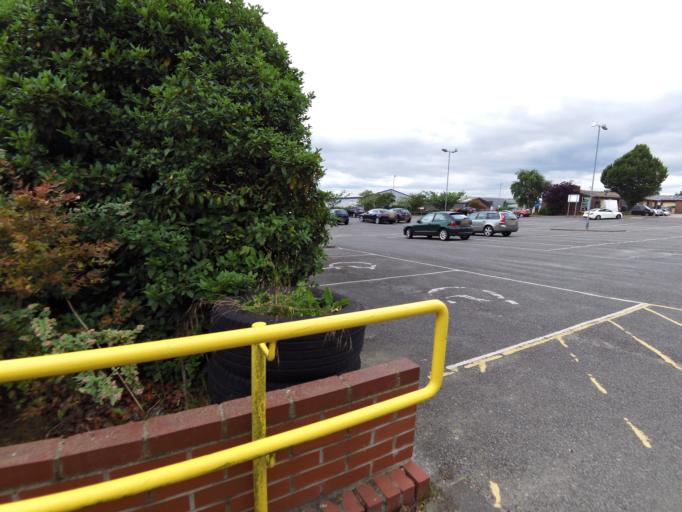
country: GB
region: England
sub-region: Norfolk
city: Diss
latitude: 52.3740
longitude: 1.1237
